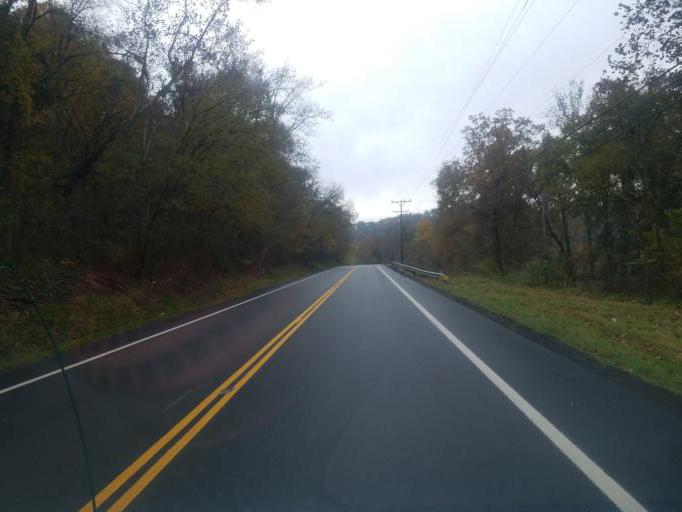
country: US
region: Ohio
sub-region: Washington County
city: Devola
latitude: 39.5374
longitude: -81.5455
